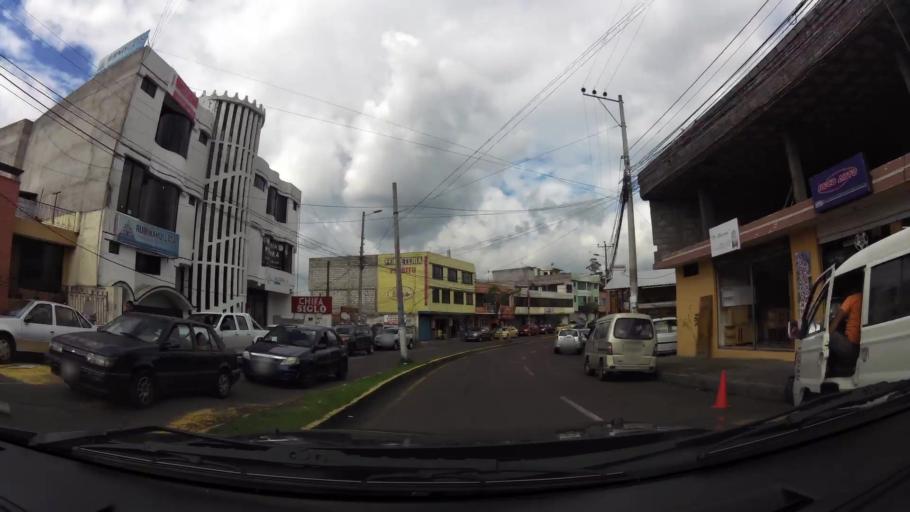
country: EC
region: Pichincha
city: Sangolqui
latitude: -0.3253
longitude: -78.4479
